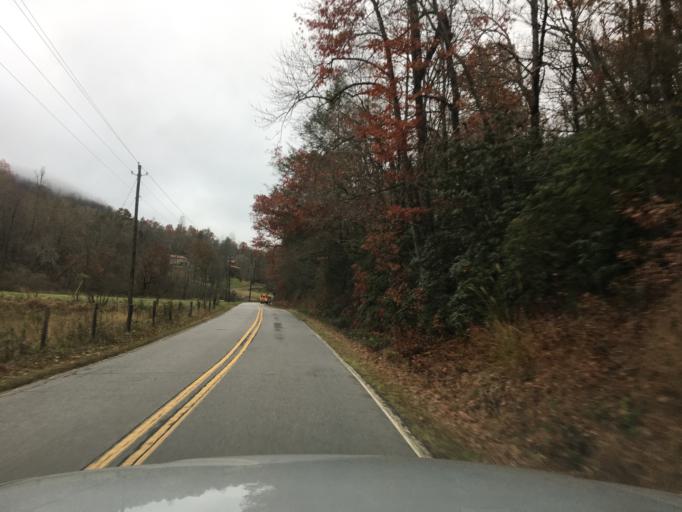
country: US
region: North Carolina
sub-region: Rutherford County
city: Lake Lure
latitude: 35.5291
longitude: -82.2420
